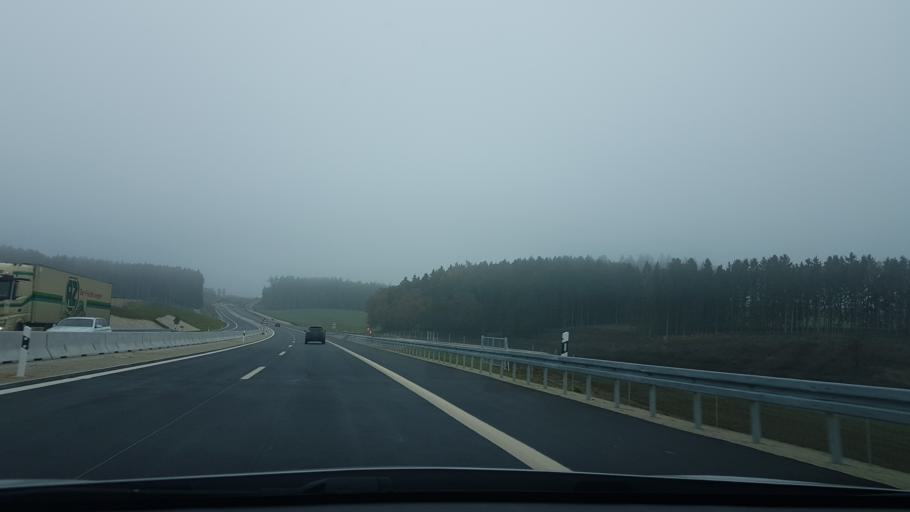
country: DE
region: Bavaria
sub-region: Lower Bavaria
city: Essenbach
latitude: 48.6447
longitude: 12.1994
